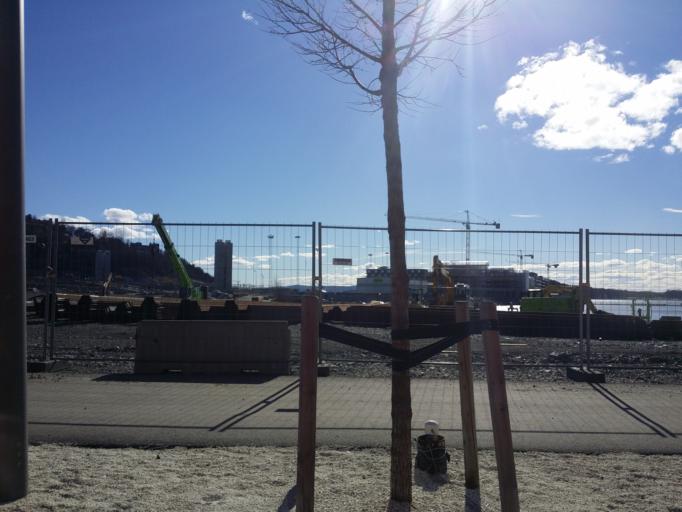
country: NO
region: Oslo
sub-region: Oslo
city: Oslo
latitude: 59.9070
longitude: 10.7611
